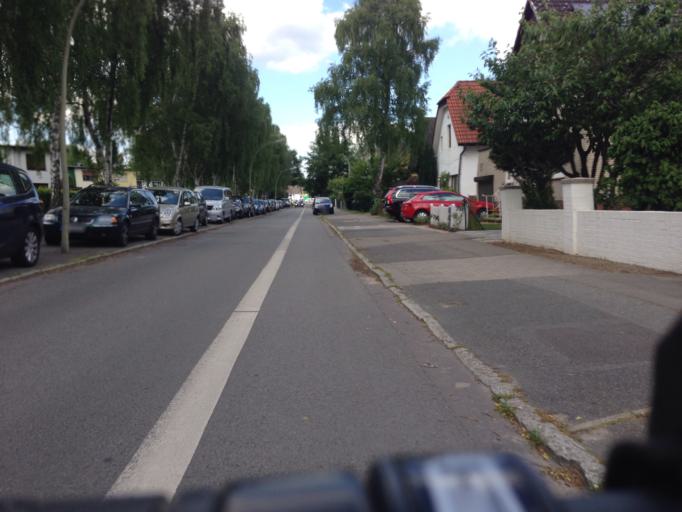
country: DE
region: Hamburg
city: Farmsen-Berne
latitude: 53.5912
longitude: 10.1393
